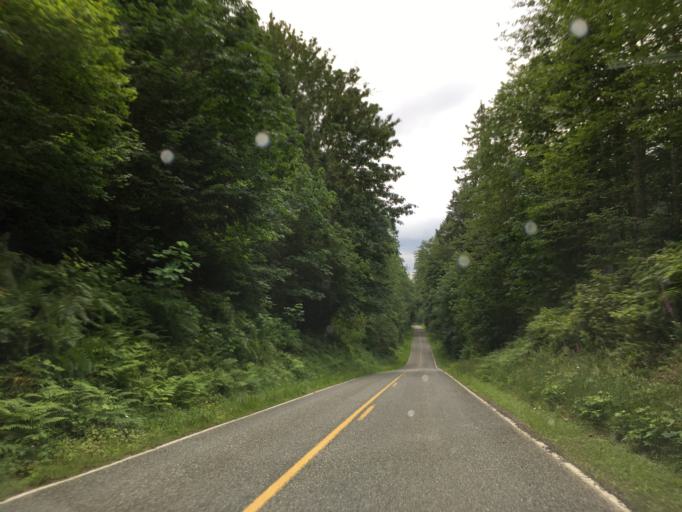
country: US
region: Washington
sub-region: Whatcom County
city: Peaceful Valley
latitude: 48.9989
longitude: -122.0784
